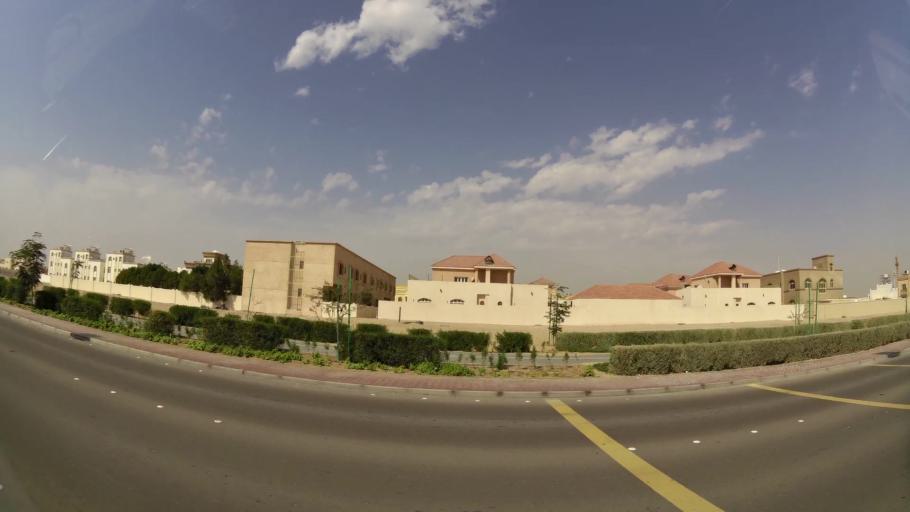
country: AE
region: Abu Dhabi
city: Abu Dhabi
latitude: 24.3252
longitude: 54.5542
